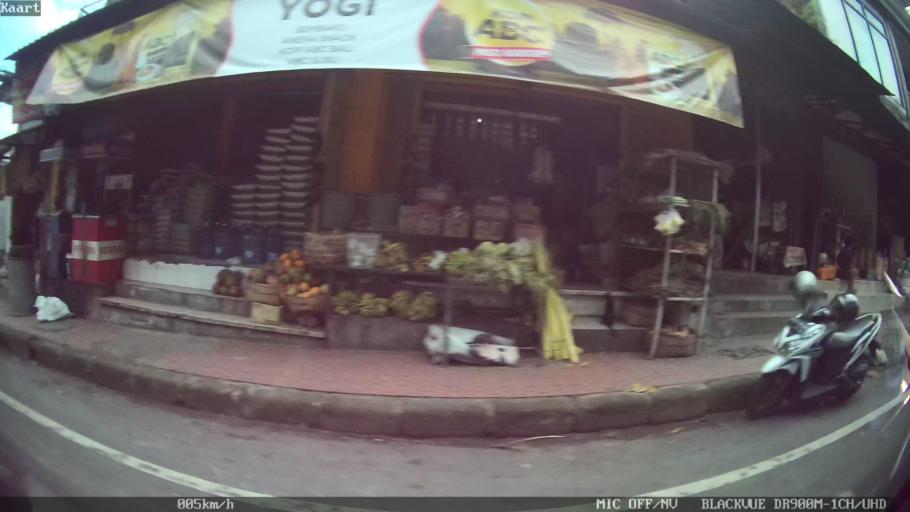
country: ID
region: Bali
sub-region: Kabupaten Gianyar
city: Ubud
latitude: -8.5347
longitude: 115.3127
